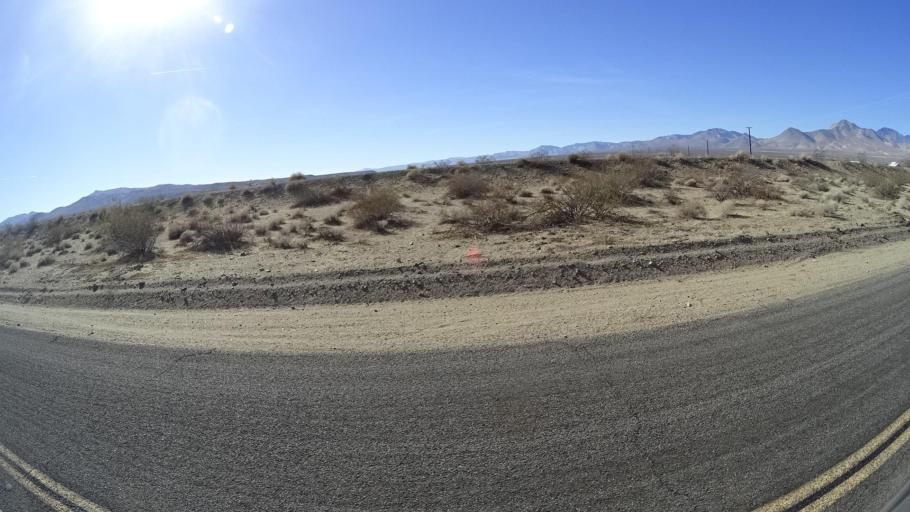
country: US
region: California
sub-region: Kern County
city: Inyokern
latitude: 35.5932
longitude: -117.7952
